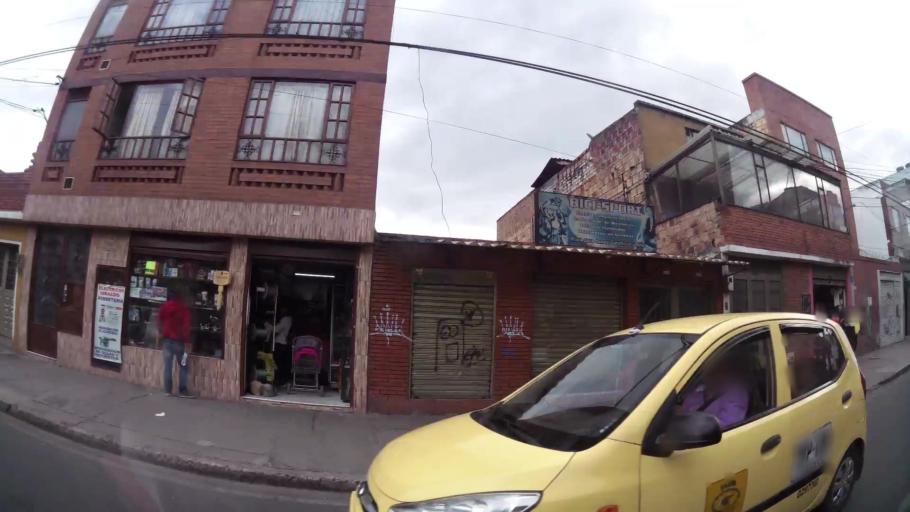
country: CO
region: Bogota D.C.
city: Barrio San Luis
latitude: 4.7043
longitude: -74.1094
